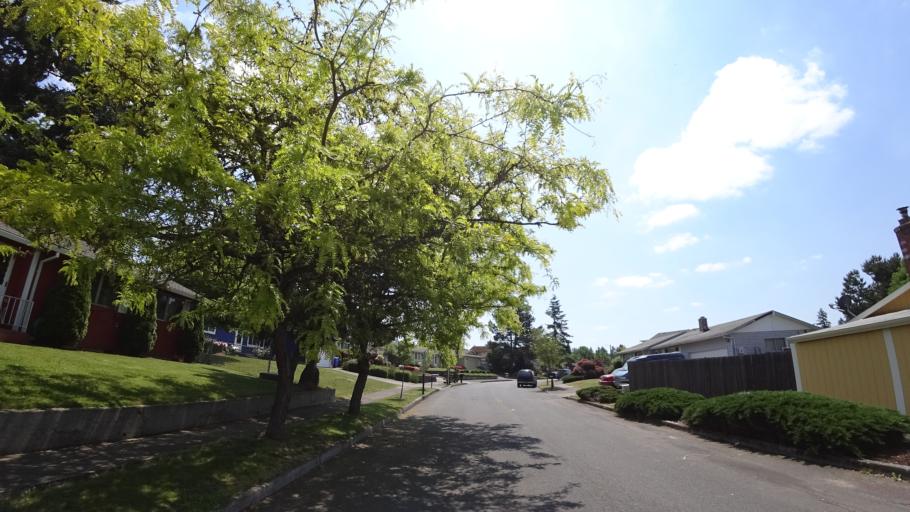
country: US
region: Oregon
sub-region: Multnomah County
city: Fairview
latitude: 45.5387
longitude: -122.4981
